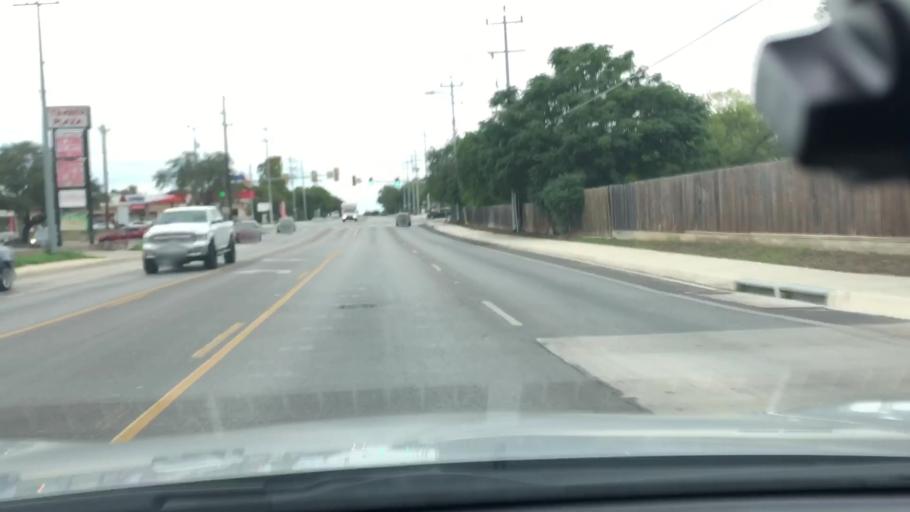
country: US
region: Texas
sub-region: Bexar County
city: Leon Valley
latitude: 29.4891
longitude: -98.6655
